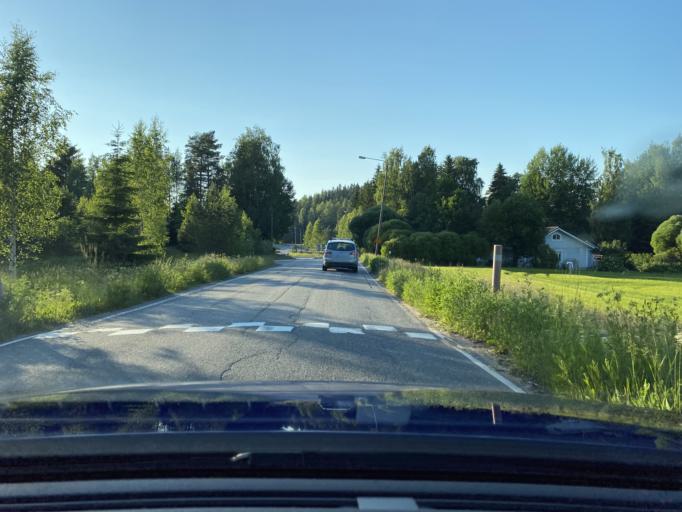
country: FI
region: Haeme
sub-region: Haemeenlinna
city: Tervakoski
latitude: 60.7427
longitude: 24.6499
